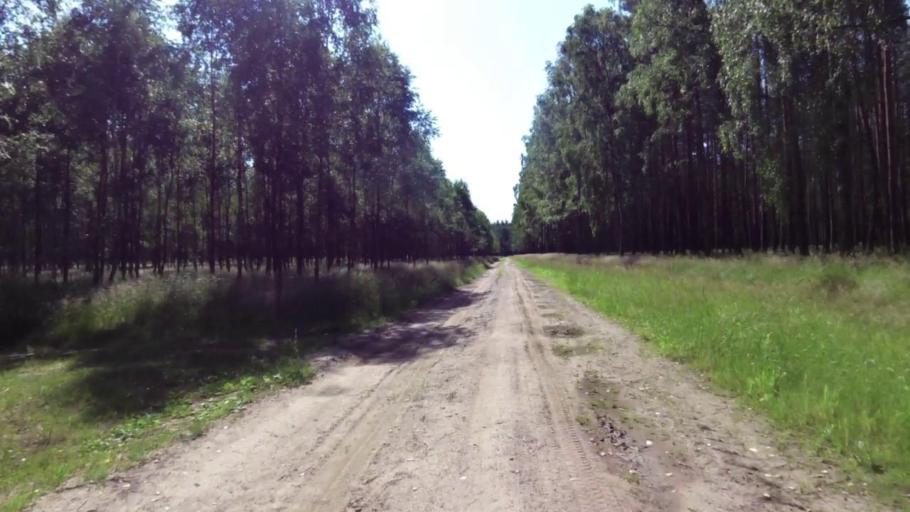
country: PL
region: West Pomeranian Voivodeship
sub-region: Powiat swidwinski
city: Polczyn-Zdroj
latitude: 53.8710
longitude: 16.1166
